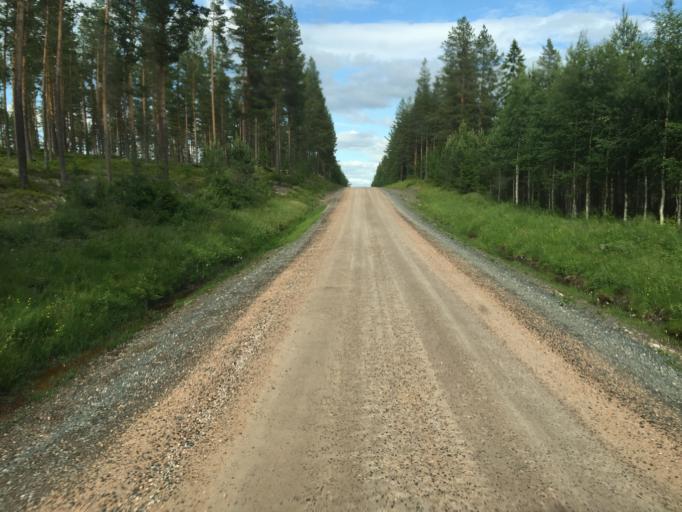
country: SE
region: Dalarna
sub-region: Malung-Saelens kommun
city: Malung
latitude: 60.9177
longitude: 13.7807
